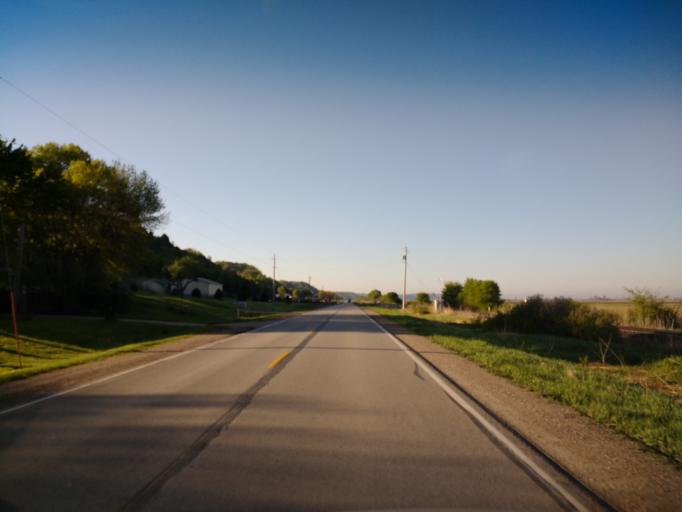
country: US
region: Iowa
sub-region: Harrison County
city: Missouri Valley
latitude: 41.4776
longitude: -95.8829
